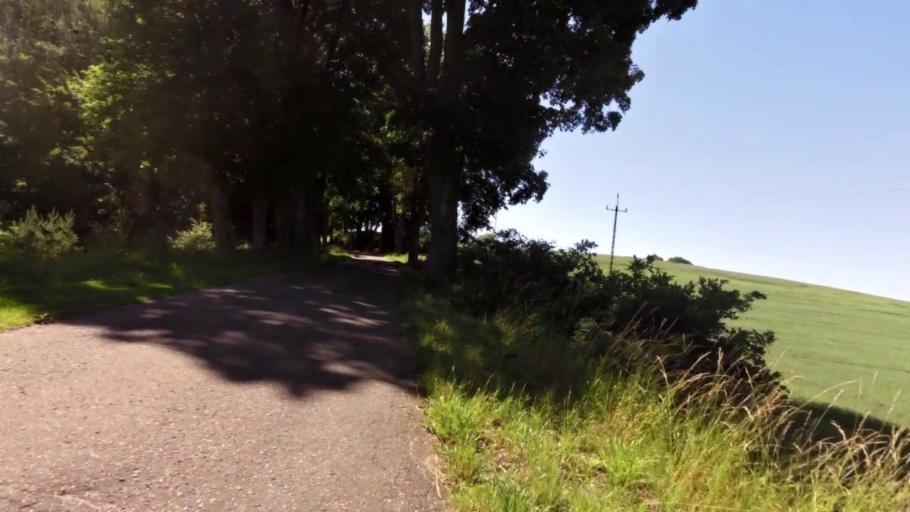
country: PL
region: West Pomeranian Voivodeship
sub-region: Powiat swidwinski
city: Rabino
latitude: 53.8546
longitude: 15.9773
